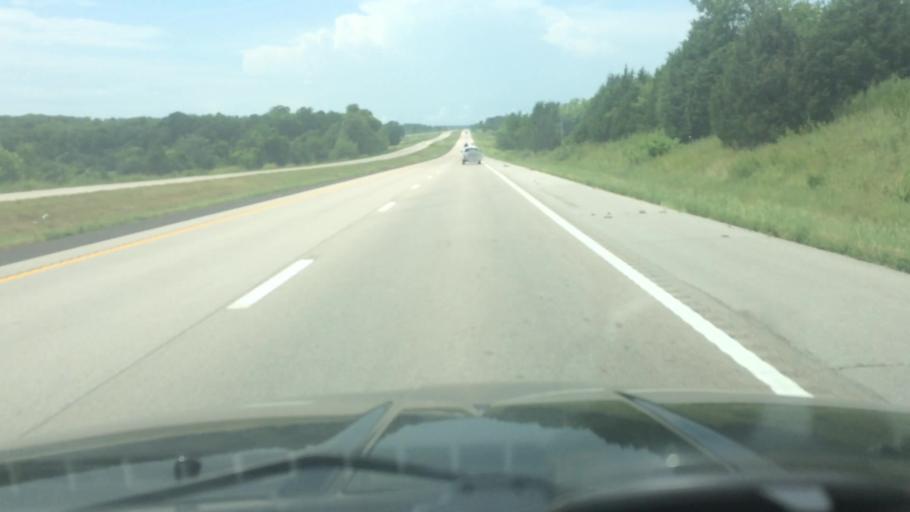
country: US
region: Missouri
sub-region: Polk County
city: Humansville
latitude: 37.7840
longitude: -93.5786
